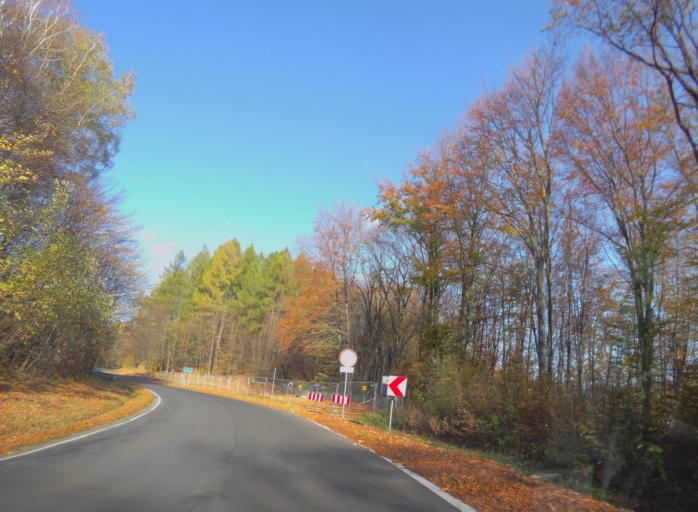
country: PL
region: Subcarpathian Voivodeship
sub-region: Powiat leski
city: Polanczyk
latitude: 49.3950
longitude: 22.4377
